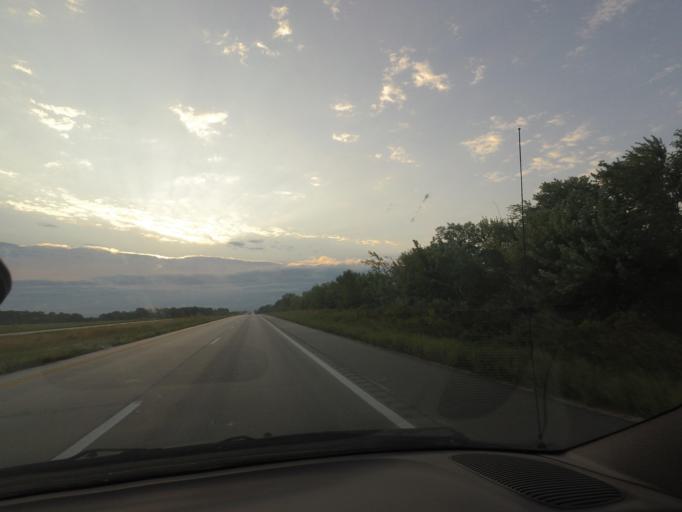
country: US
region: Missouri
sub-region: Shelby County
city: Shelbina
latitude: 39.7343
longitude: -92.2142
